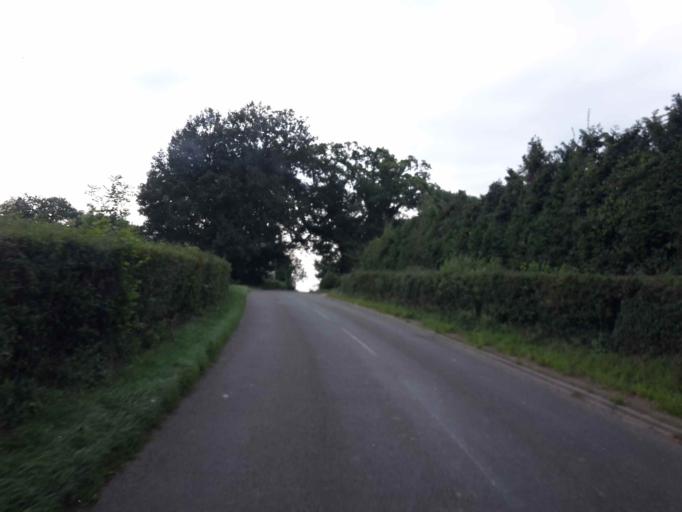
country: GB
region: England
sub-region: West Sussex
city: Billingshurst
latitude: 51.0506
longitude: -0.4330
